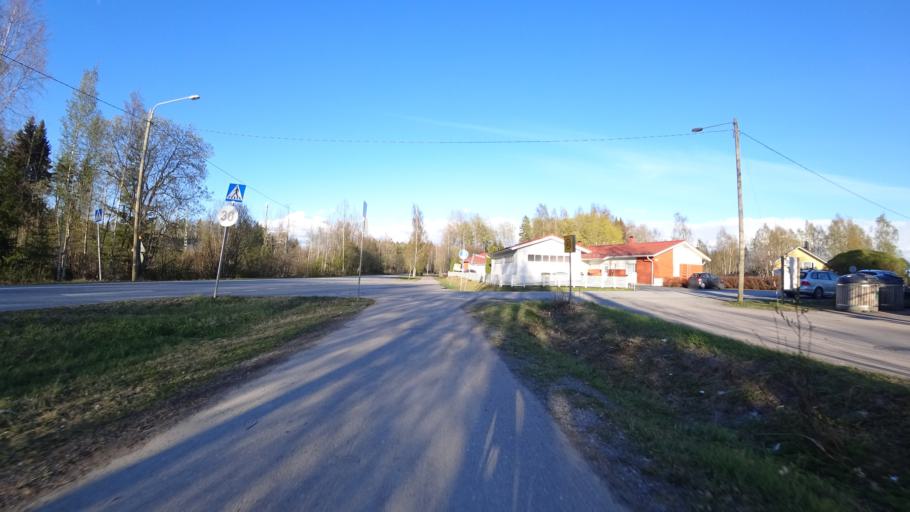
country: FI
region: Pirkanmaa
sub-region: Tampere
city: Nokia
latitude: 61.4912
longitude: 23.5436
